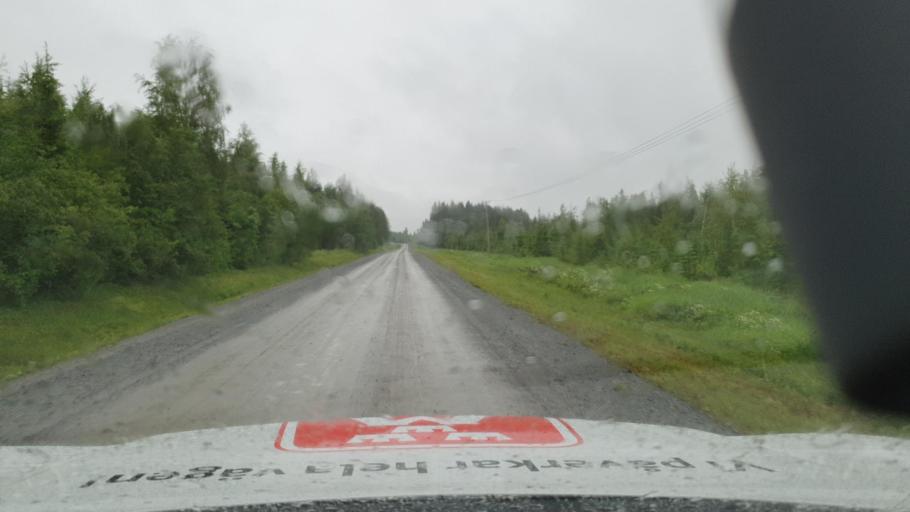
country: SE
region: Vaesterbotten
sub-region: Bjurholms Kommun
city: Bjurholm
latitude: 63.8918
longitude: 19.4184
